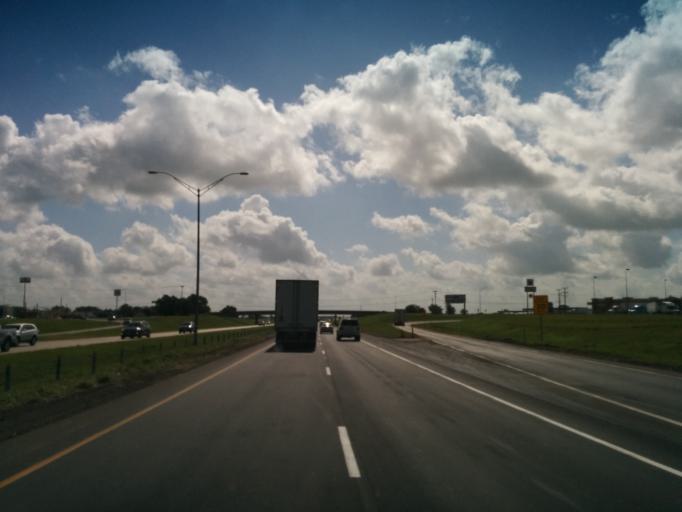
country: US
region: Texas
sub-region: Colorado County
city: Weimar
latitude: 29.6914
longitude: -96.7795
